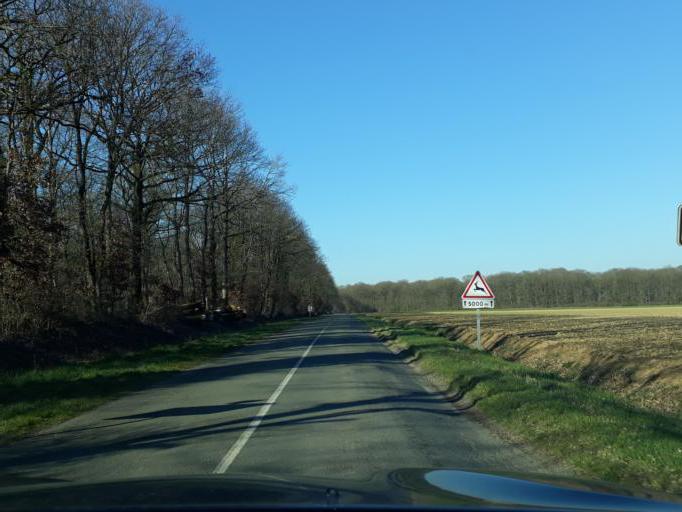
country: FR
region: Centre
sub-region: Departement du Loir-et-Cher
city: Oucques
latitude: 47.8408
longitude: 1.3815
